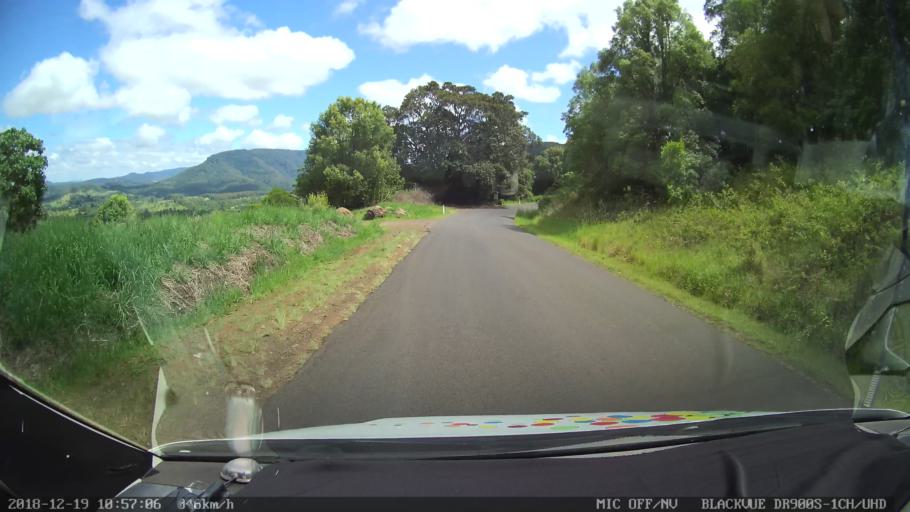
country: AU
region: New South Wales
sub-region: Lismore Municipality
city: Nimbin
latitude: -28.5898
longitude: 153.2613
